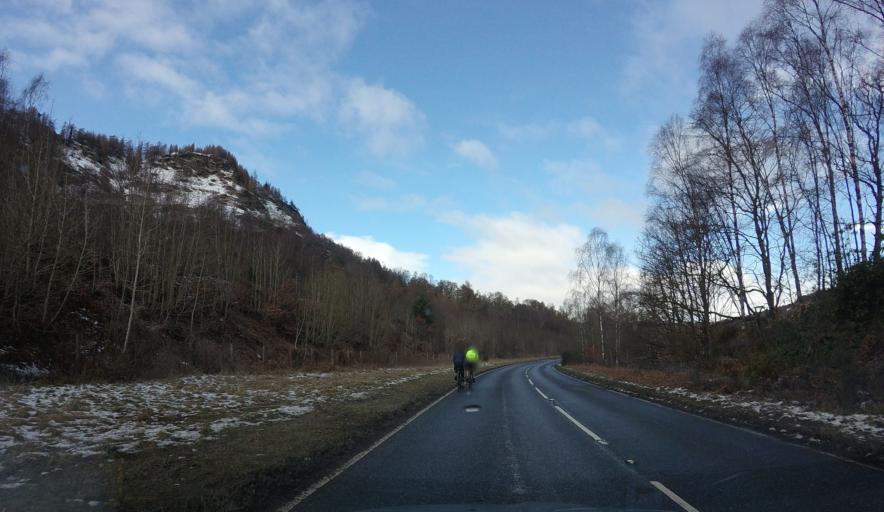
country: GB
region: Scotland
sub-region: Perth and Kinross
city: Bankfoot
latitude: 56.5468
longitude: -3.5615
